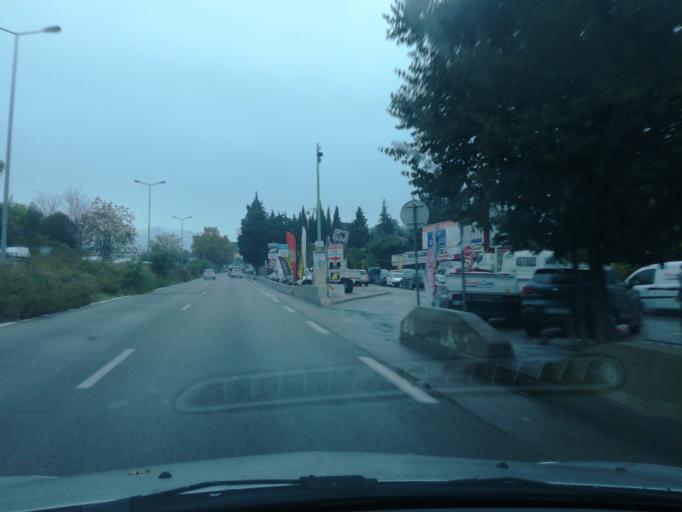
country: FR
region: Provence-Alpes-Cote d'Azur
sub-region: Departement des Alpes-Maritimes
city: Le Cannet
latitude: 43.5797
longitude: 7.0113
